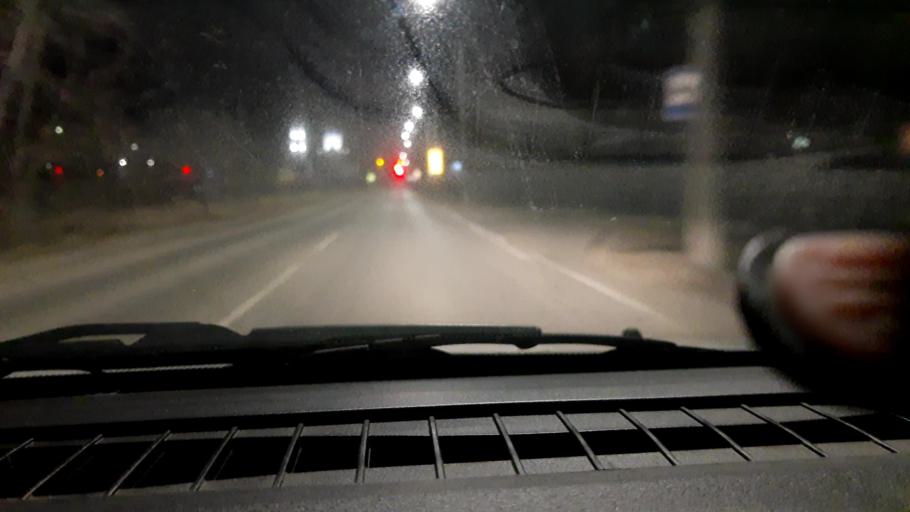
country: RU
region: Nizjnij Novgorod
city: Dzerzhinsk
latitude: 56.2427
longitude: 43.4222
